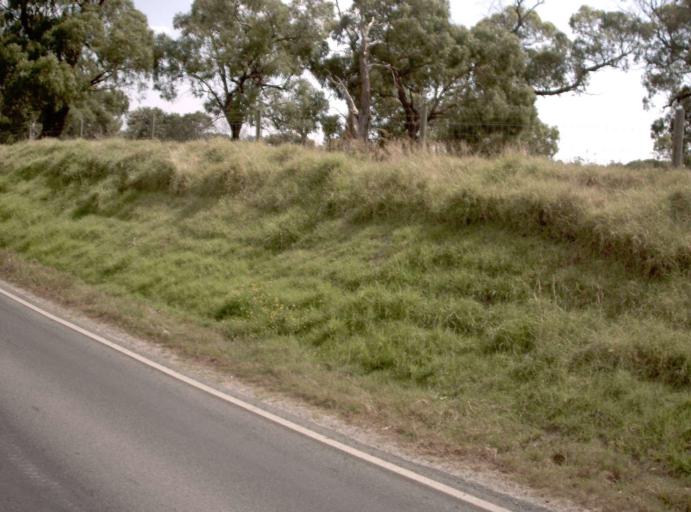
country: AU
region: Victoria
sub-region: Casey
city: Junction Village
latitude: -38.1429
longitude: 145.3223
